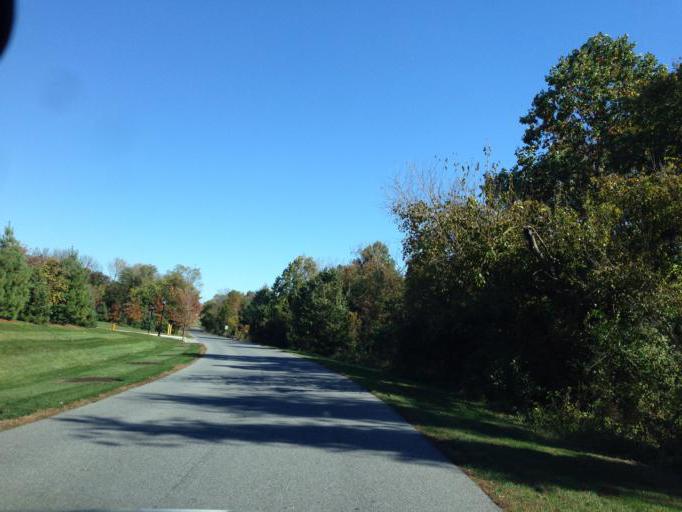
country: US
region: Maryland
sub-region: Howard County
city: Riverside
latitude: 39.1524
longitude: -76.8962
